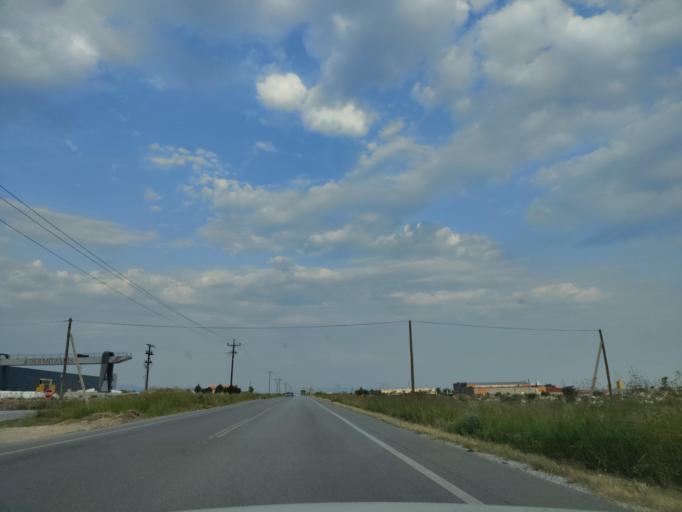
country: GR
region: East Macedonia and Thrace
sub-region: Nomos Dramas
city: Petroussa
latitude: 41.1786
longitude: 23.9951
